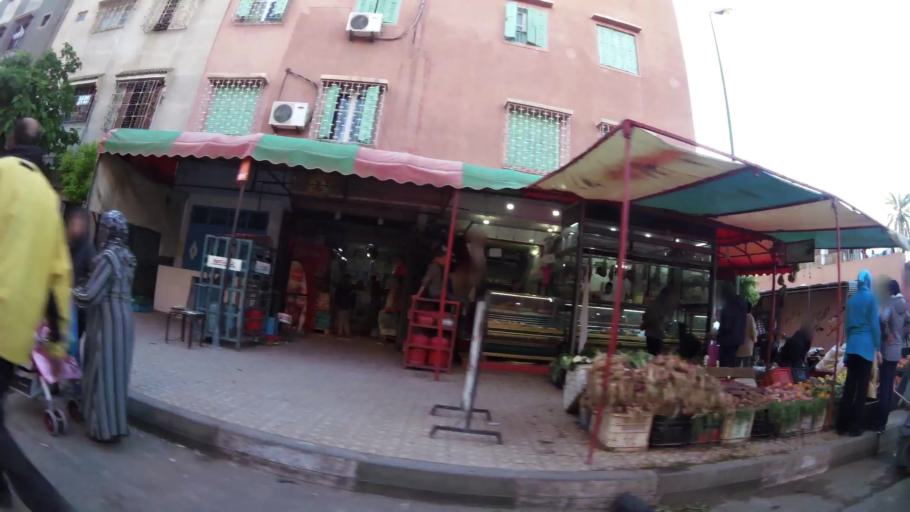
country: MA
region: Marrakech-Tensift-Al Haouz
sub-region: Marrakech
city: Marrakesh
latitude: 31.6388
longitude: -8.0365
